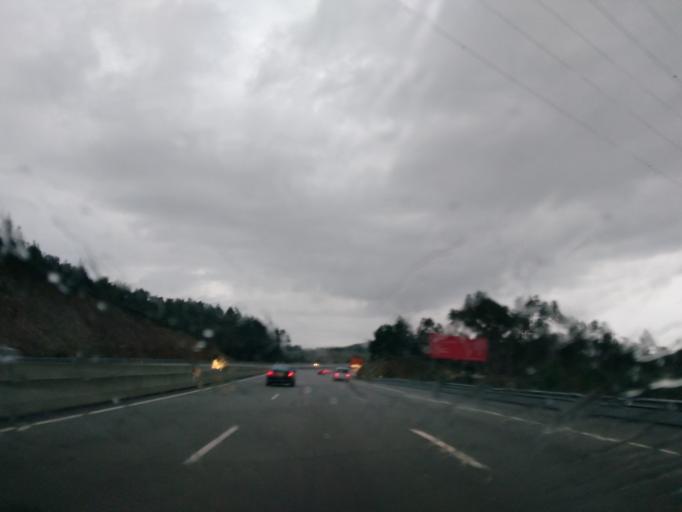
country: PT
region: Porto
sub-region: Trofa
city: Bougado
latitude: 41.3084
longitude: -8.5270
